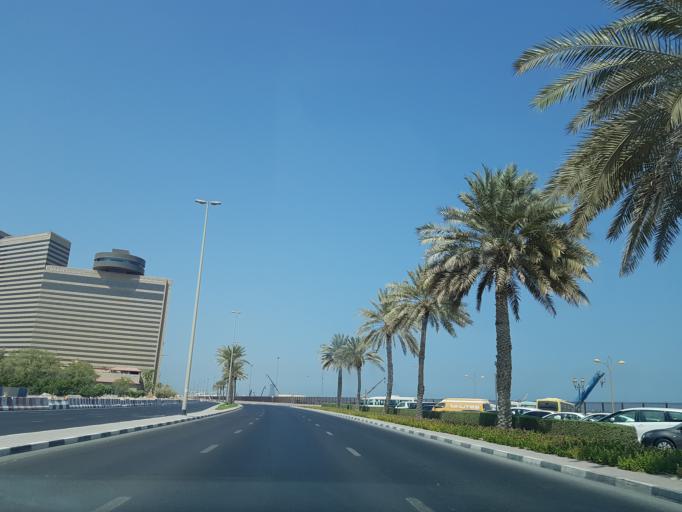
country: AE
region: Ash Shariqah
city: Sharjah
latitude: 25.2810
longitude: 55.3073
